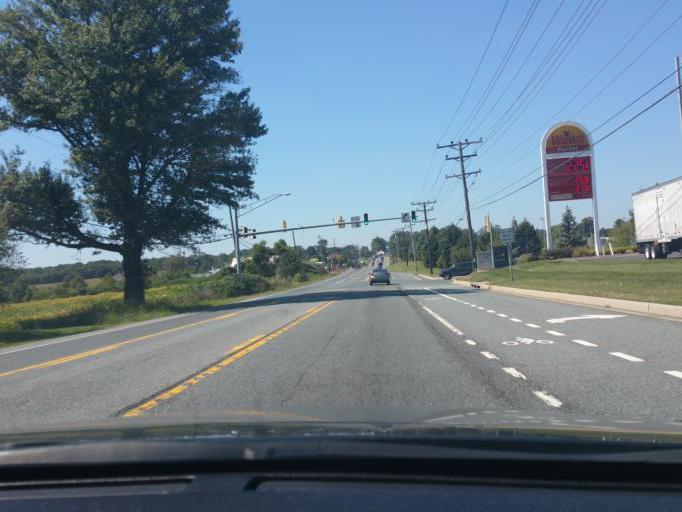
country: US
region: Maryland
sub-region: Harford County
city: South Bel Air
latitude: 39.5553
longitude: -76.2779
